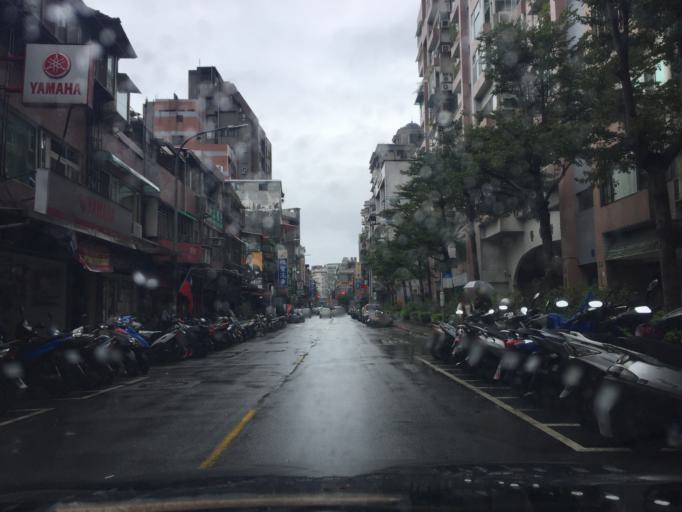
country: TW
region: Taipei
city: Taipei
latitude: 25.0787
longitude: 121.5953
